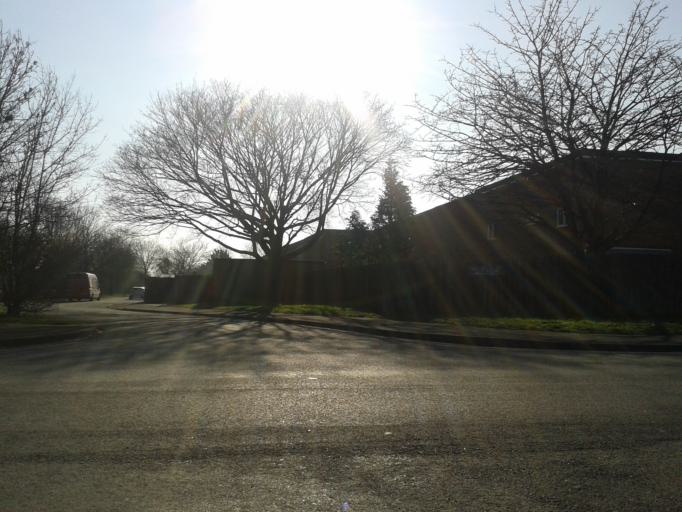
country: GB
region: England
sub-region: Cambridgeshire
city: Histon
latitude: 52.2308
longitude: 0.1279
